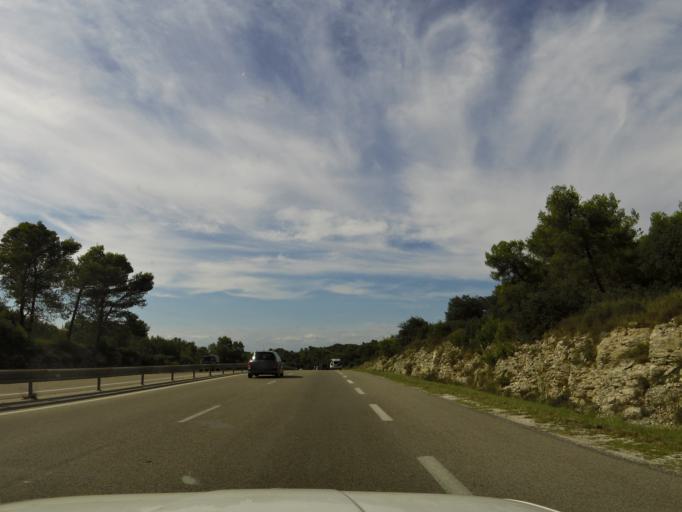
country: FR
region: Languedoc-Roussillon
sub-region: Departement du Gard
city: La Calmette
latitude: 43.8814
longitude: 4.3093
